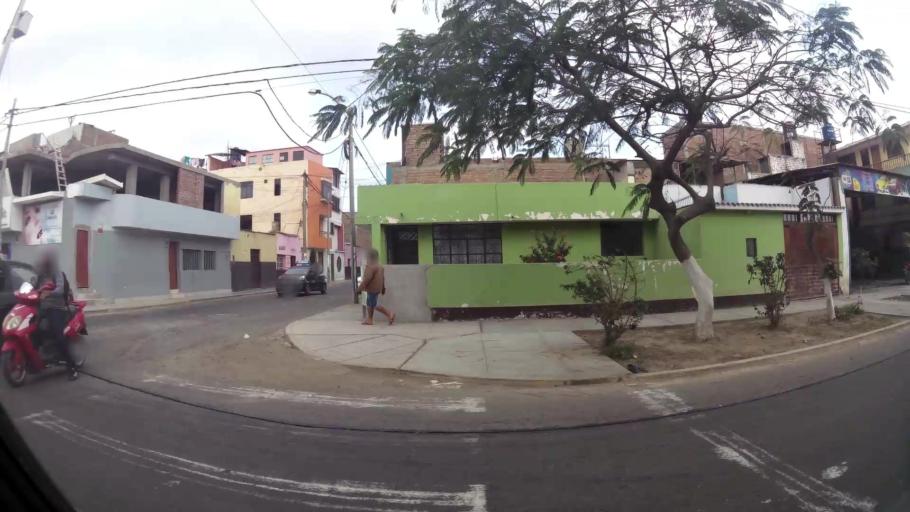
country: PE
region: La Libertad
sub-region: Provincia de Trujillo
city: Trujillo
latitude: -8.1012
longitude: -79.0222
